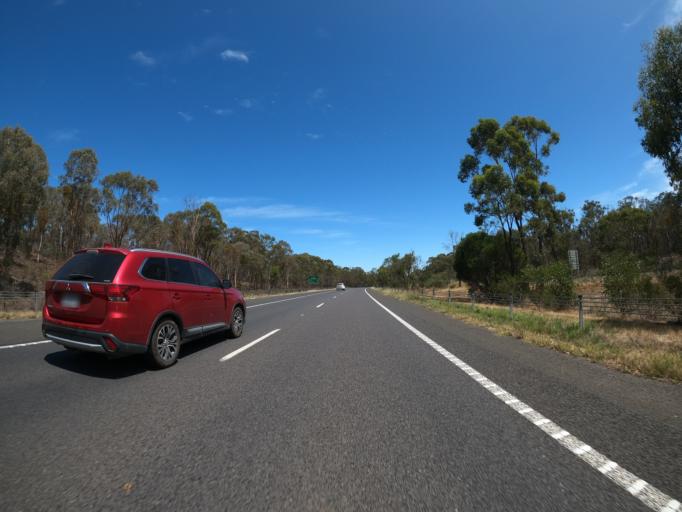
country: AU
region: Victoria
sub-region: Benalla
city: Benalla
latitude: -36.5819
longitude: 145.9505
